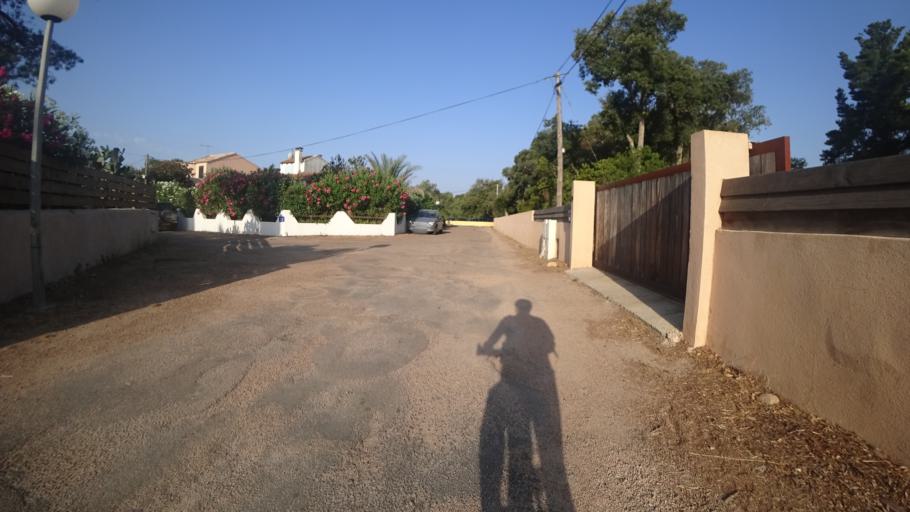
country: FR
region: Corsica
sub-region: Departement de la Corse-du-Sud
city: Porto-Vecchio
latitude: 41.6399
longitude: 9.3455
